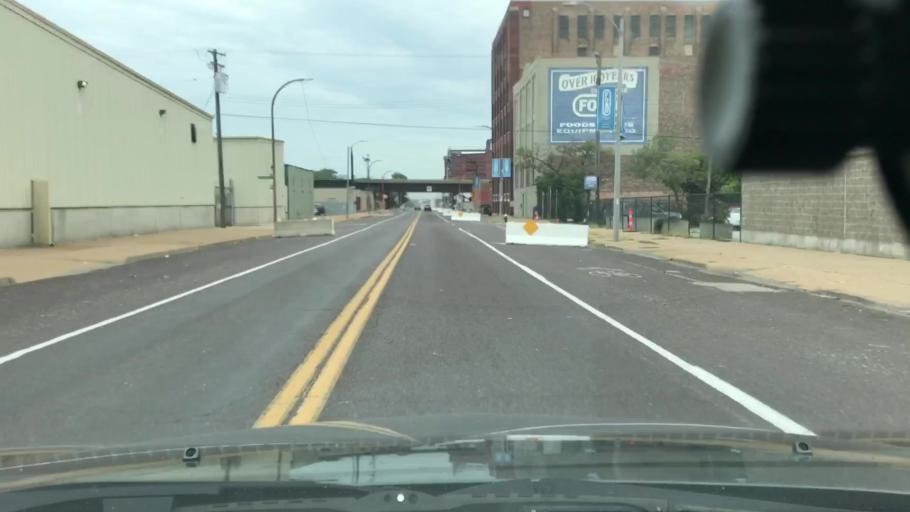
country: US
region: Missouri
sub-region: City of Saint Louis
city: St. Louis
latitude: 38.6482
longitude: -90.1883
